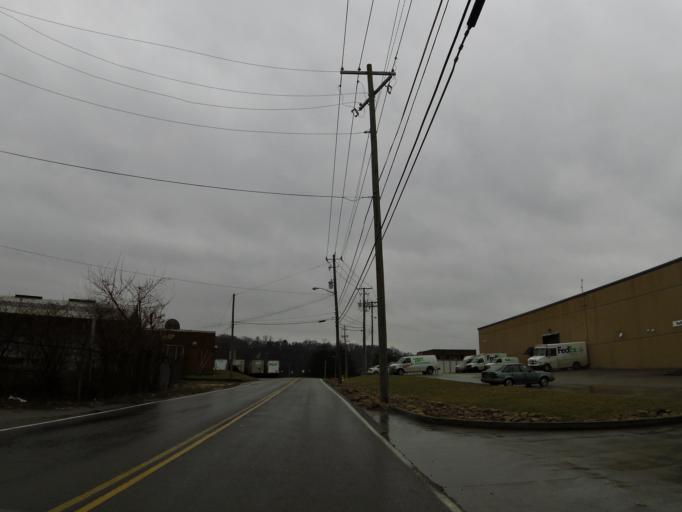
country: US
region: Tennessee
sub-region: Knox County
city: Knoxville
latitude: 35.9772
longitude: -83.9653
